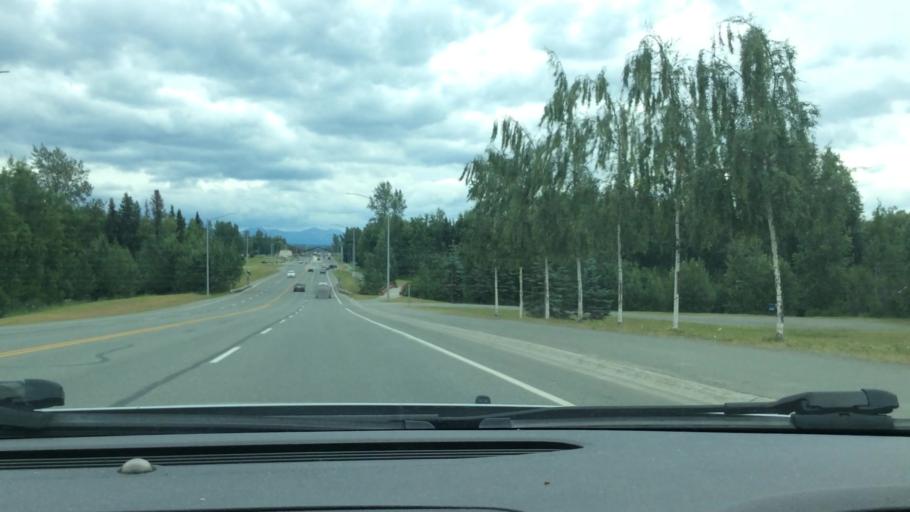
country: US
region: Alaska
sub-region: Anchorage Municipality
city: Anchorage
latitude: 61.2387
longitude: -149.7786
